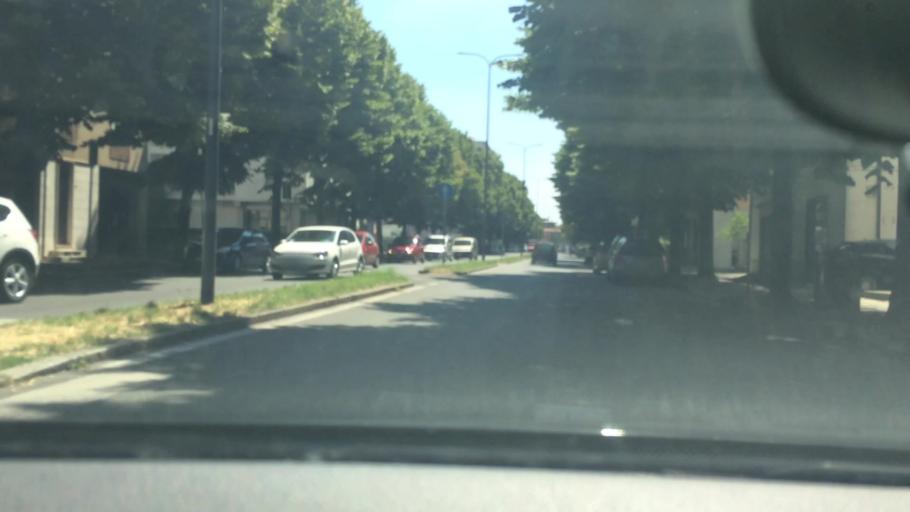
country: IT
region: Emilia-Romagna
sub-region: Provincia di Piacenza
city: Piacenza
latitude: 45.0444
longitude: 9.6740
